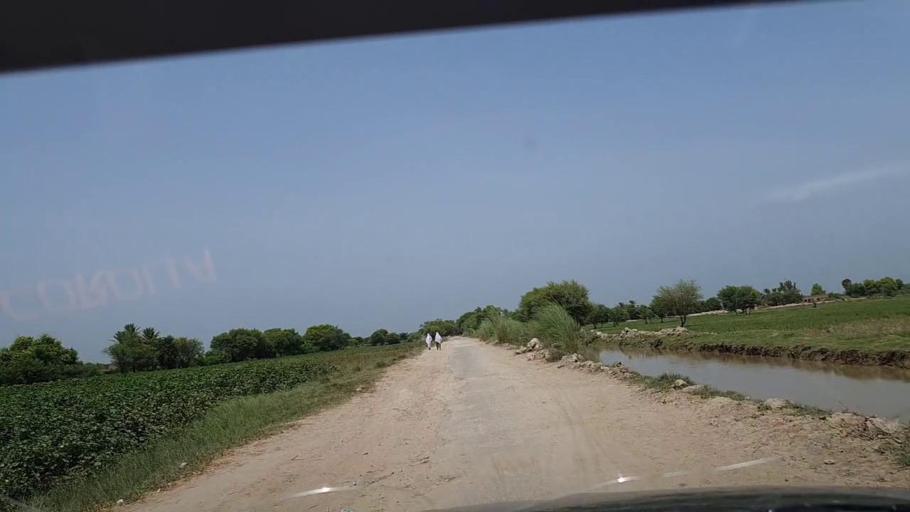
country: PK
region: Sindh
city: Khanpur
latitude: 27.8082
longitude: 69.4505
